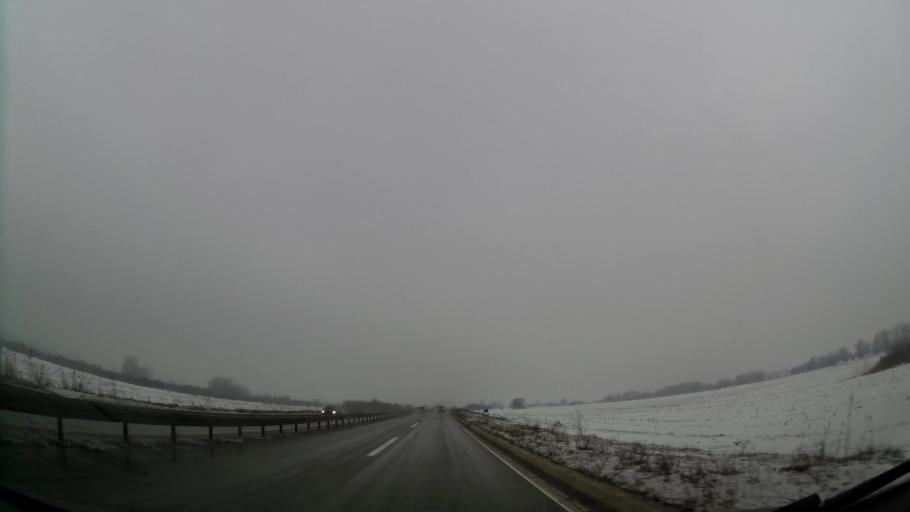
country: RS
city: Ostruznica
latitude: 44.7470
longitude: 20.3705
